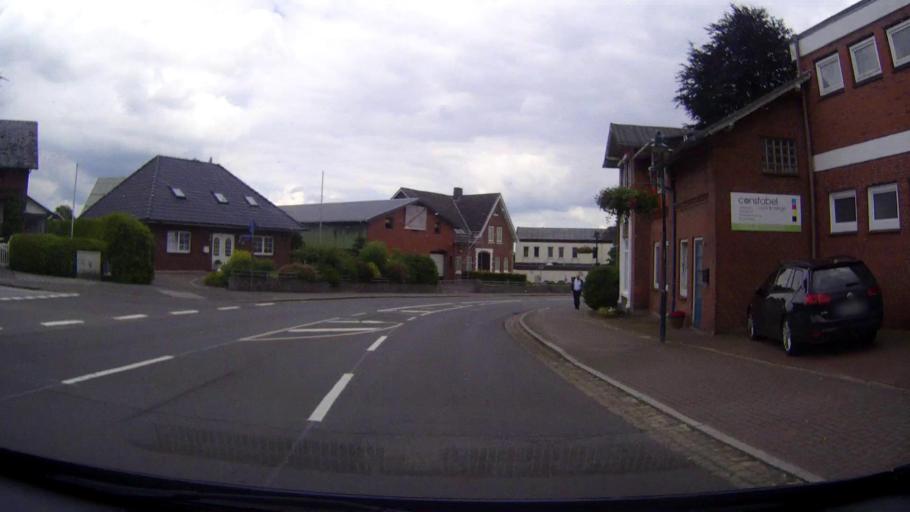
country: DE
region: Schleswig-Holstein
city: Hanerau-Hademarschen
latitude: 54.1275
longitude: 9.4110
